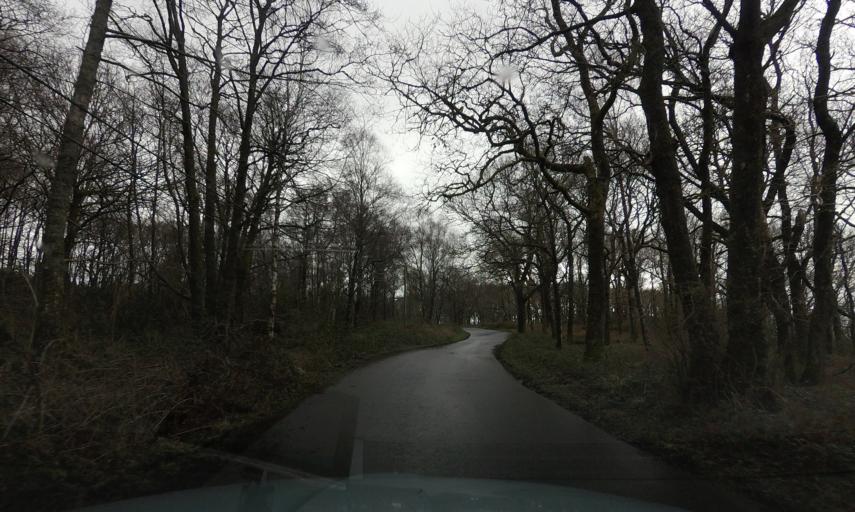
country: GB
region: Scotland
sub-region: West Dunbartonshire
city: Balloch
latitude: 56.1234
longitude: -4.5990
